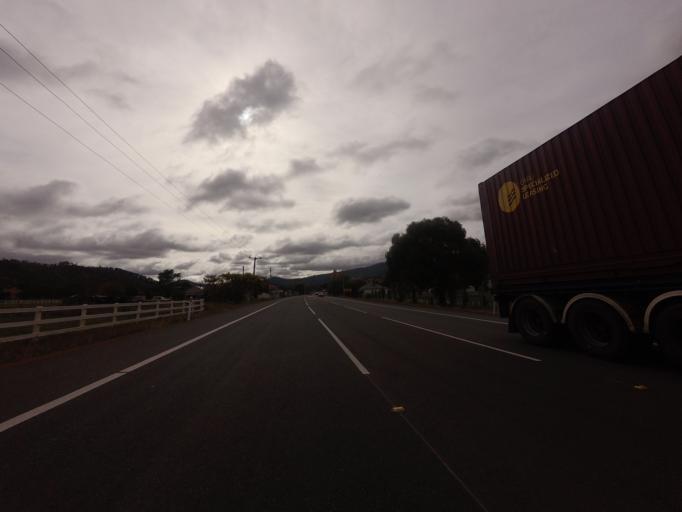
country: AU
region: Tasmania
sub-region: Brighton
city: Bridgewater
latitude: -42.6185
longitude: 147.2220
